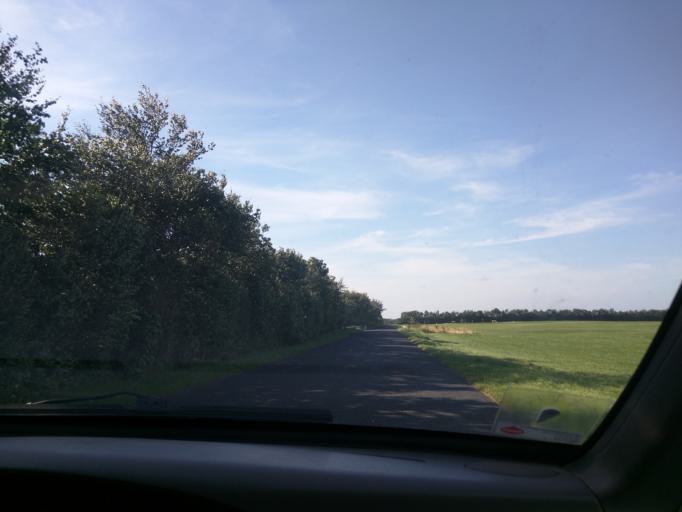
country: DK
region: Central Jutland
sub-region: Viborg Kommune
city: Bjerringbro
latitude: 56.4885
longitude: 9.5946
